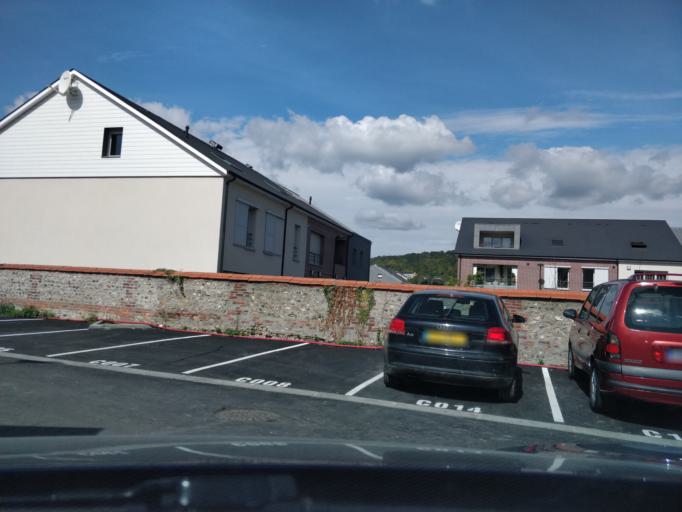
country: FR
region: Haute-Normandie
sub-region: Departement de la Seine-Maritime
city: Saint-Leger-du-Bourg-Denis
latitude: 49.4353
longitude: 1.1514
